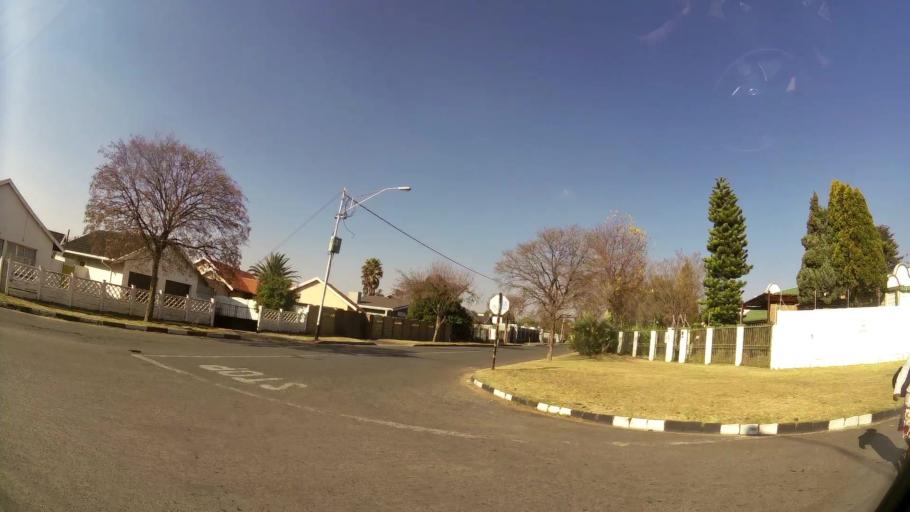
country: ZA
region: Gauteng
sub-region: City of Johannesburg Metropolitan Municipality
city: Johannesburg
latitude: -26.2529
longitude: 28.0091
